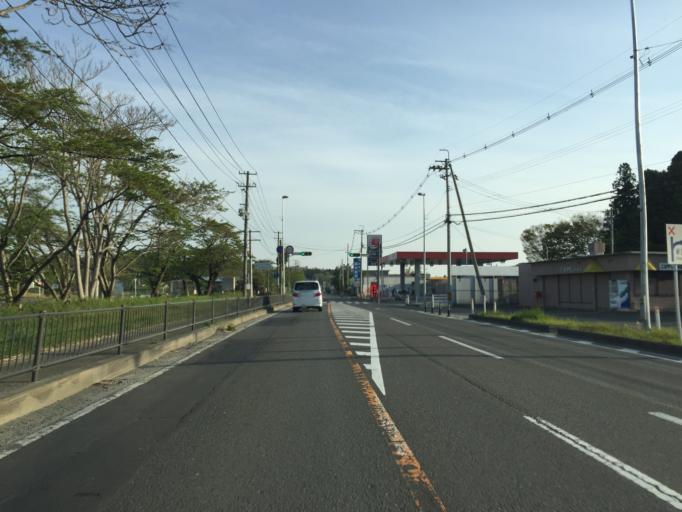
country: JP
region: Miyagi
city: Watari
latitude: 37.9412
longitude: 140.8942
